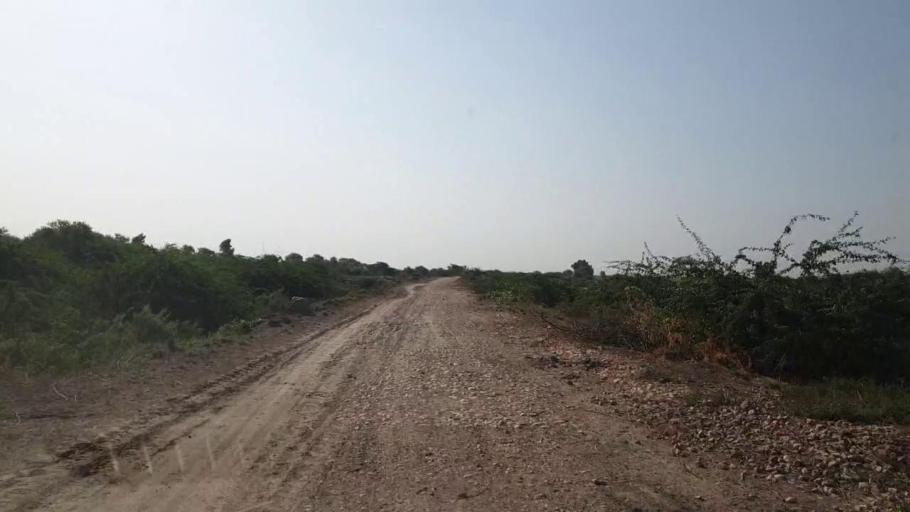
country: PK
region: Sindh
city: Kadhan
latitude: 24.6211
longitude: 69.0730
